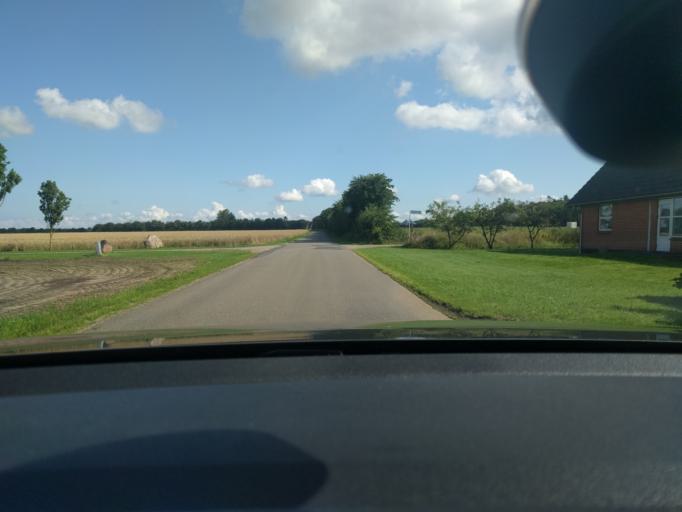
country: DK
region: Central Jutland
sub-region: Viborg Kommune
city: Stoholm
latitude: 56.4780
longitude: 9.2666
